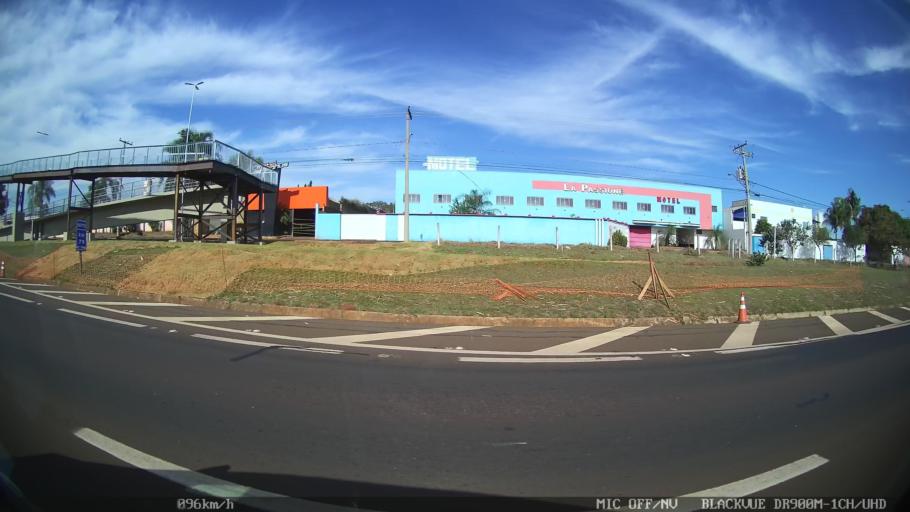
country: BR
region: Sao Paulo
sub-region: Araraquara
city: Araraquara
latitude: -21.8000
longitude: -48.1431
